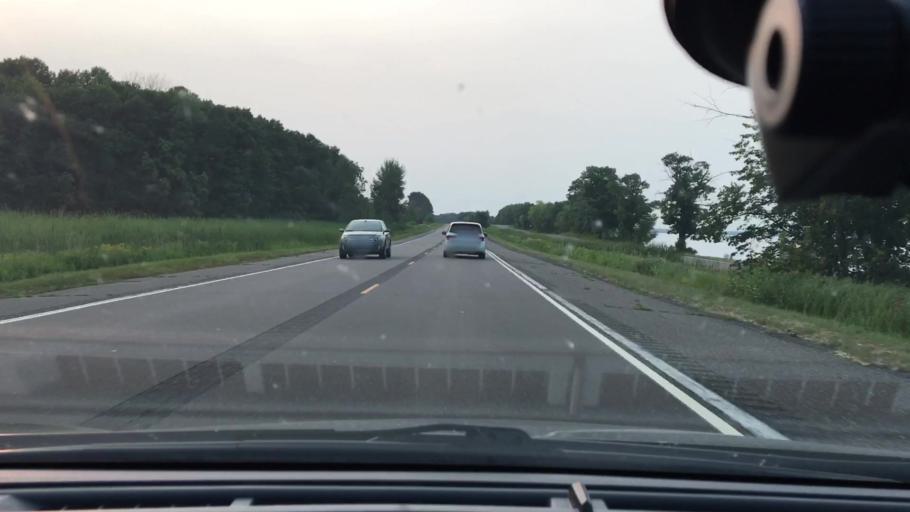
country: US
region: Minnesota
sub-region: Mille Lacs County
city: Vineland
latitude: 46.1357
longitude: -93.6942
